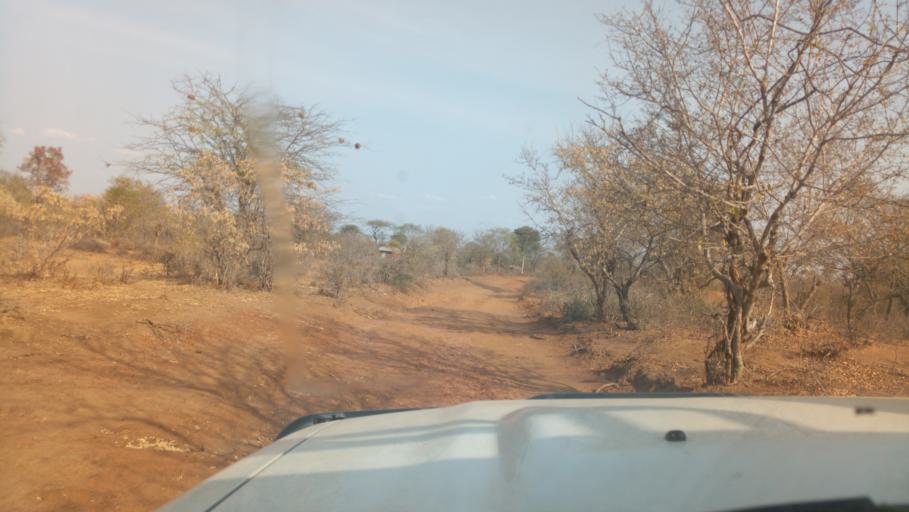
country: KE
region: Kitui
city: Kitui
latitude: -1.5785
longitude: 37.9223
